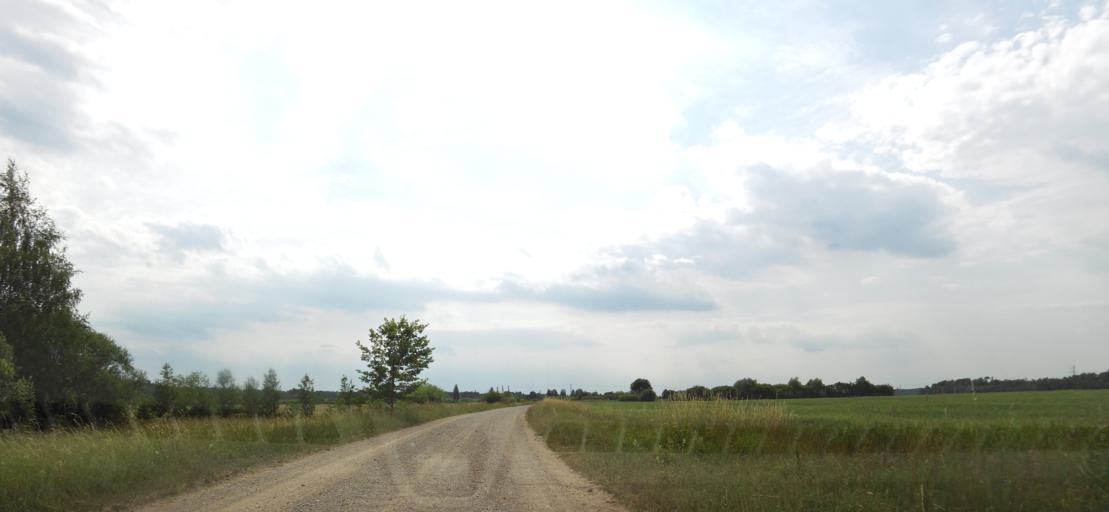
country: LT
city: Obeliai
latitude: 56.1866
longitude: 25.0217
